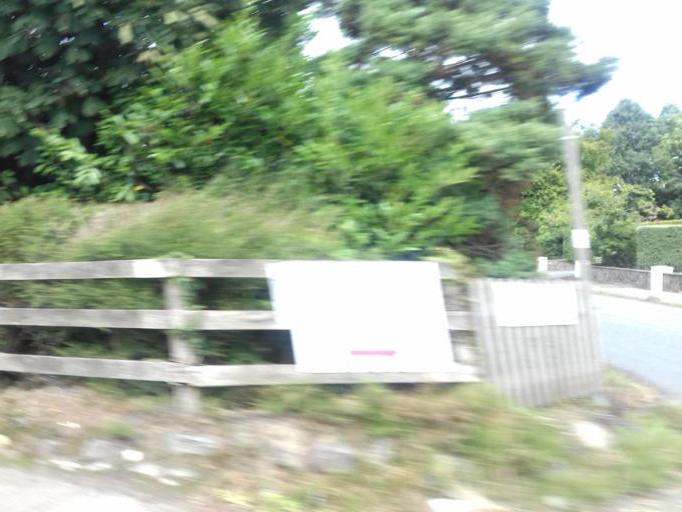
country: IE
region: Leinster
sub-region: Loch Garman
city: Enniscorthy
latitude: 52.5049
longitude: -6.5446
